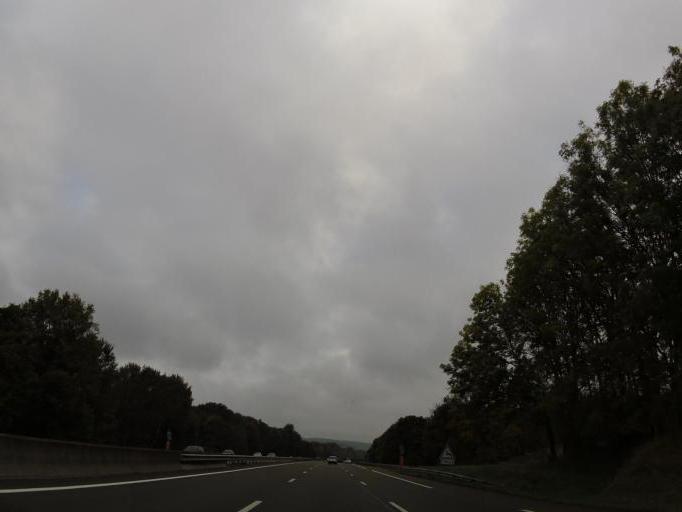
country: FR
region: Ile-de-France
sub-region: Departement de Seine-et-Marne
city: Saint-Germain-sur-Morin
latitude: 48.8642
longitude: 2.8491
